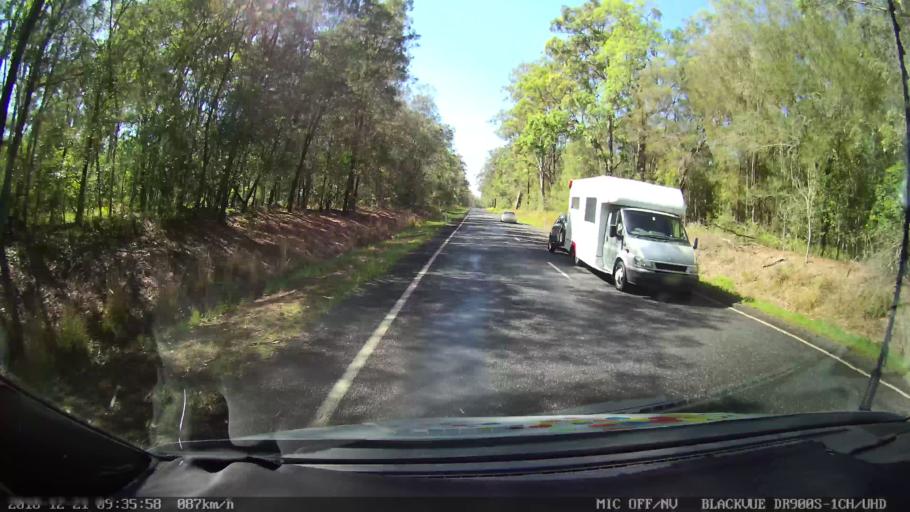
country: AU
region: New South Wales
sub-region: Clarence Valley
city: Grafton
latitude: -29.5174
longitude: 152.9812
